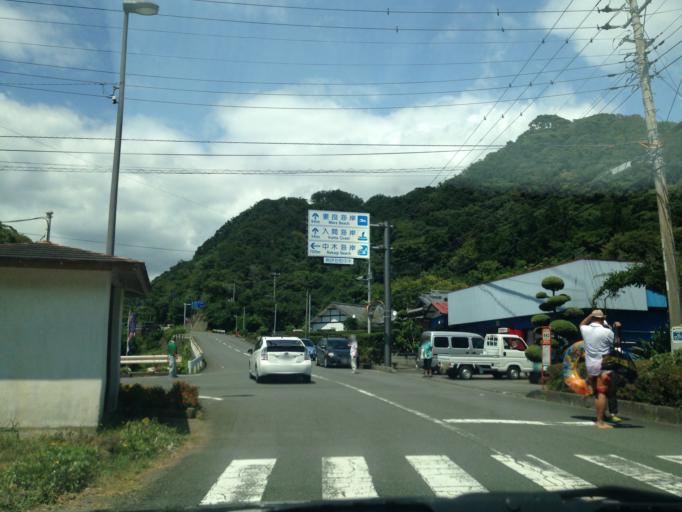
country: JP
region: Shizuoka
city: Shimoda
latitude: 34.6212
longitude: 138.8242
